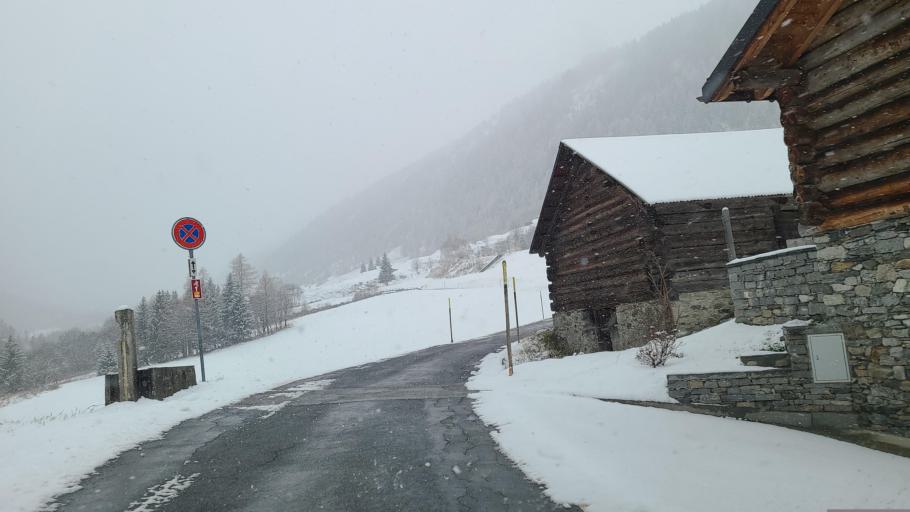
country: CH
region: Ticino
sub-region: Leventina District
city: Airolo
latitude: 46.5080
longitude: 8.5177
